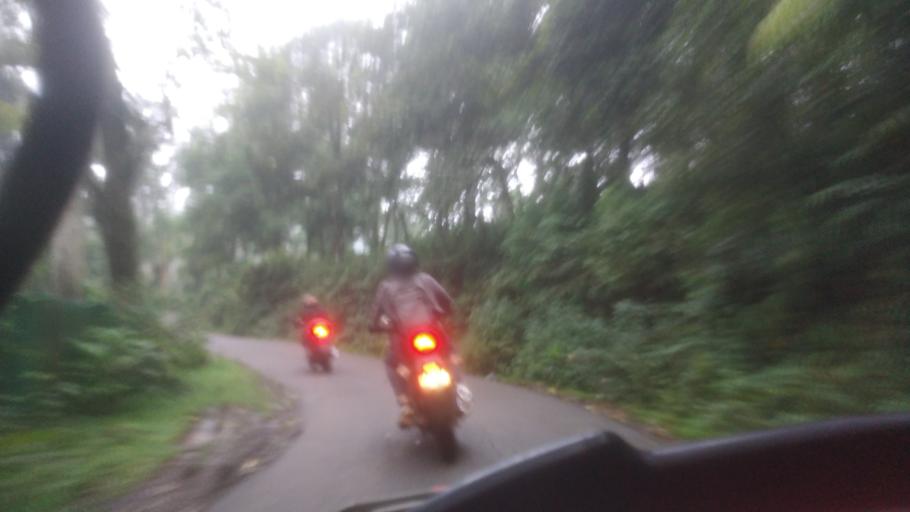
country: IN
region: Tamil Nadu
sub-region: Theni
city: Kombai
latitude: 9.8931
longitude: 77.2127
